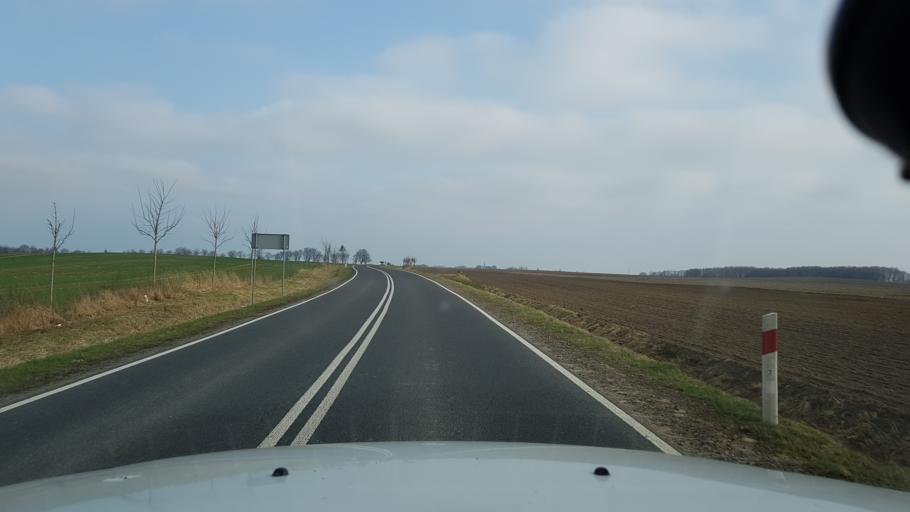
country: PL
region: West Pomeranian Voivodeship
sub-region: Powiat koszalinski
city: Sianow
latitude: 54.2749
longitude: 16.2696
